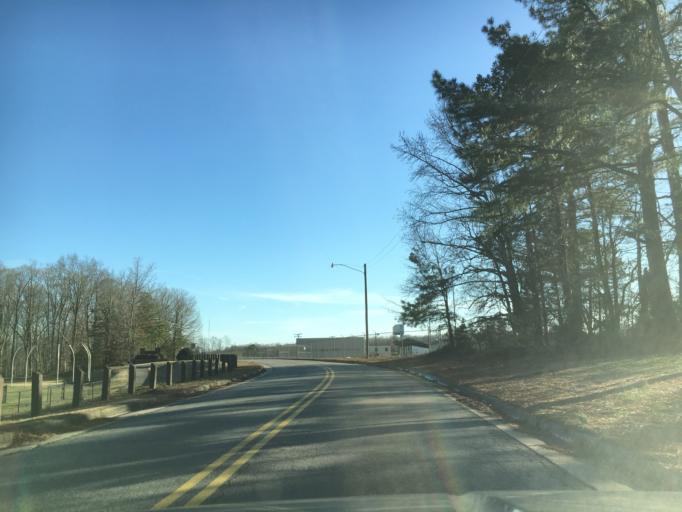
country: US
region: Virginia
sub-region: Halifax County
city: South Boston
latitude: 36.7288
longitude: -78.9145
